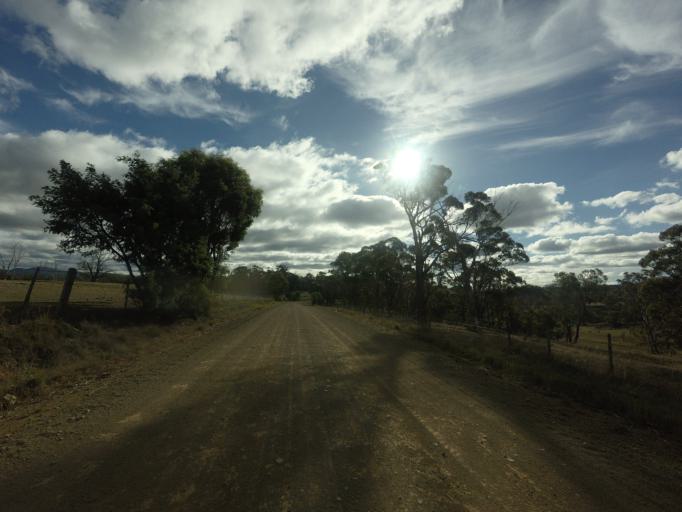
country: AU
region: Tasmania
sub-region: Brighton
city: Bridgewater
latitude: -42.4574
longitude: 147.2513
